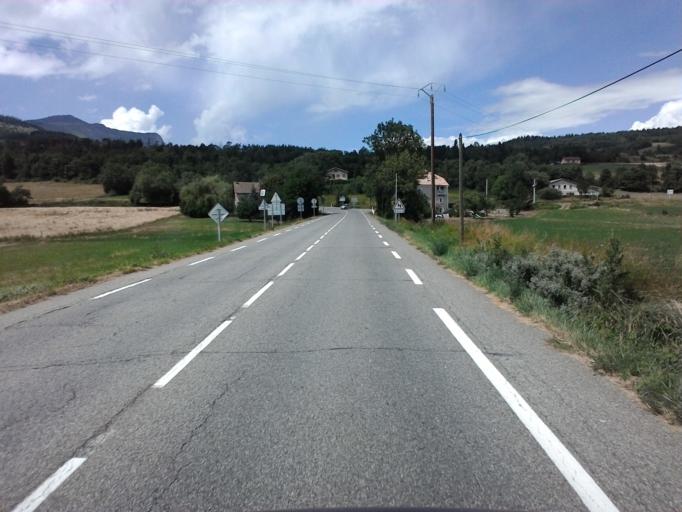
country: FR
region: Provence-Alpes-Cote d'Azur
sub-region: Departement des Hautes-Alpes
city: Gap
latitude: 44.5875
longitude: 6.0814
